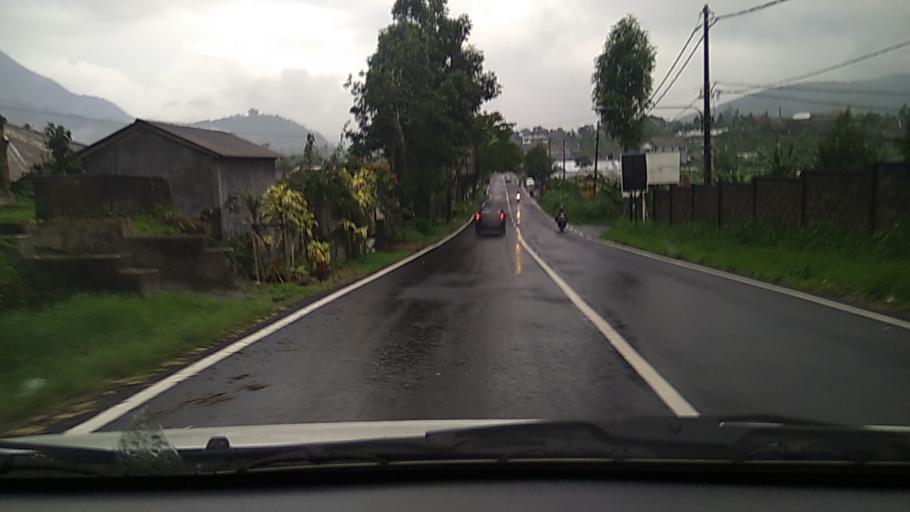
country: ID
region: Bali
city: Munduk
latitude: -8.2429
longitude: 115.1486
